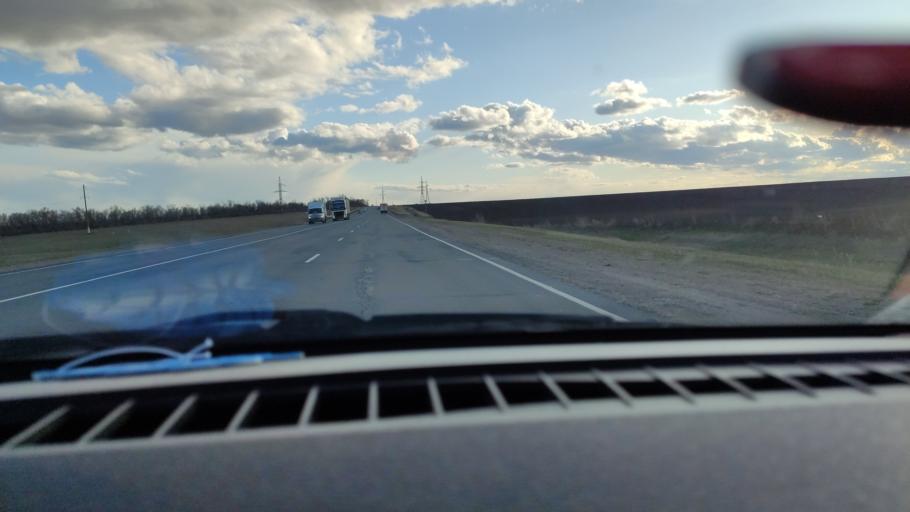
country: RU
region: Saratov
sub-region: Saratovskiy Rayon
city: Saratov
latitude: 51.7486
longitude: 46.0572
